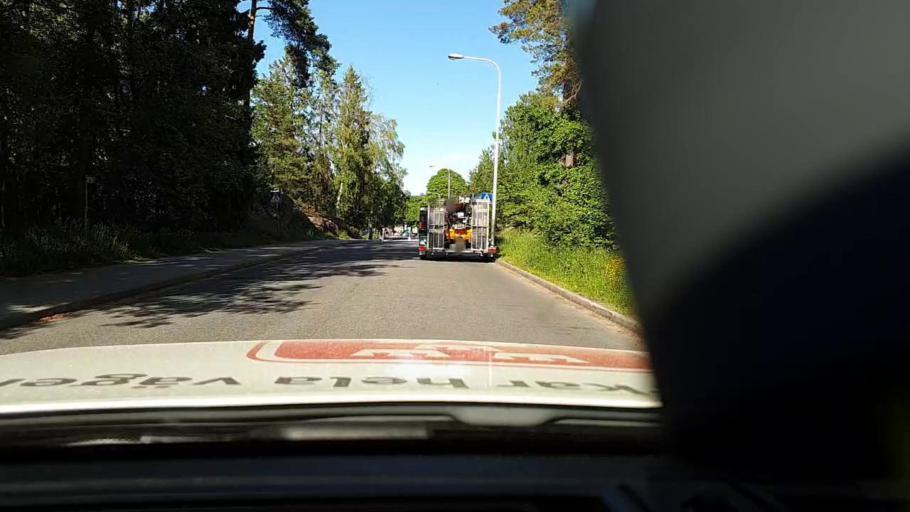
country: SE
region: Stockholm
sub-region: Stockholms Kommun
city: Arsta
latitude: 59.2538
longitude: 18.0722
